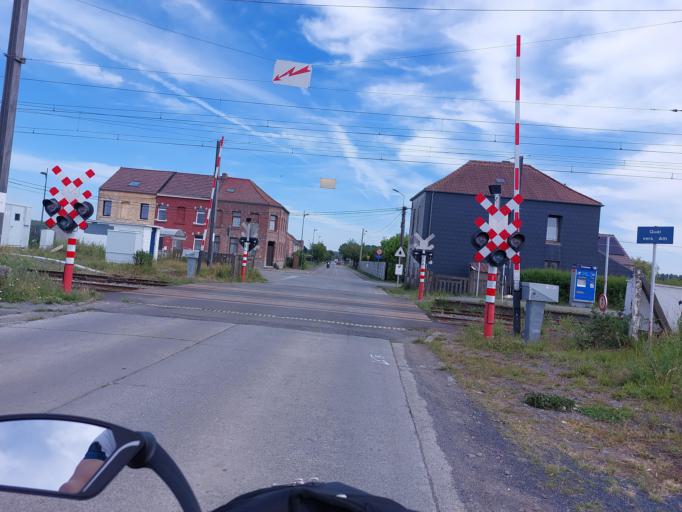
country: BE
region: Wallonia
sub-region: Province du Hainaut
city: Brugelette
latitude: 50.5997
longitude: 3.8341
